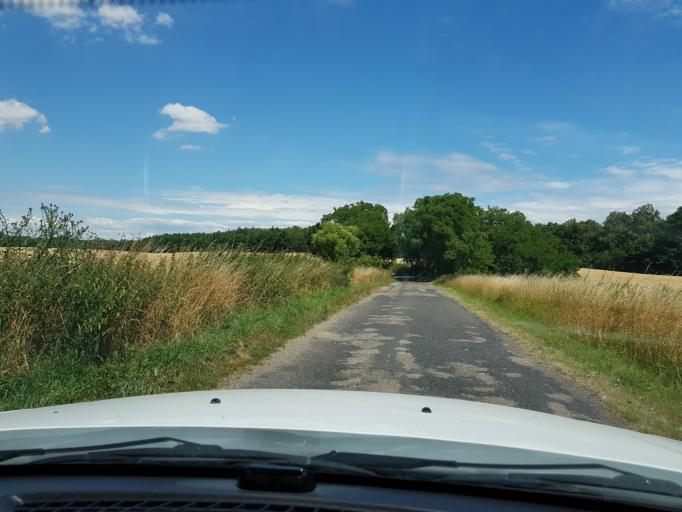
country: PL
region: West Pomeranian Voivodeship
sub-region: Powiat mysliborski
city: Barlinek
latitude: 52.9747
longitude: 15.1269
